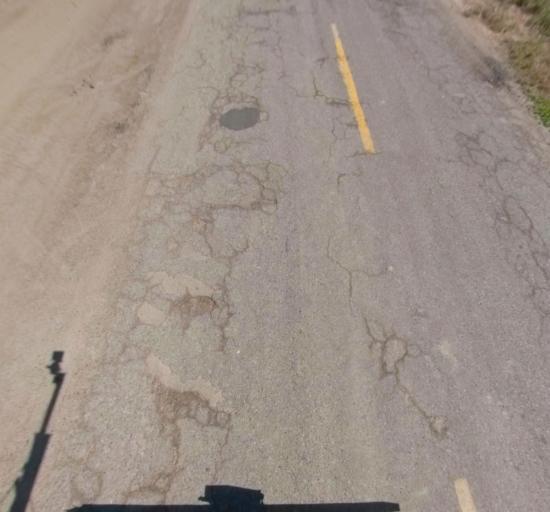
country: US
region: California
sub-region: Madera County
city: Madera
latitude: 36.9401
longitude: -120.1836
